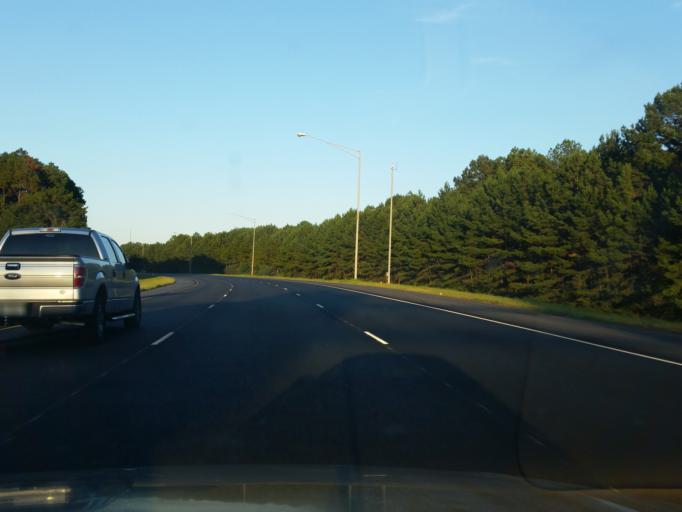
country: US
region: Alabama
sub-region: Mobile County
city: Tillmans Corner
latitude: 30.6258
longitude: -88.1200
